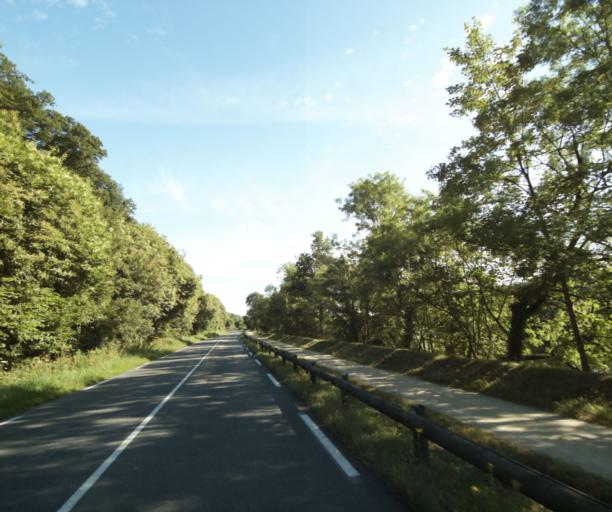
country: FR
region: Pays de la Loire
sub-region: Departement de la Mayenne
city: Laval
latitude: 48.0440
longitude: -0.7662
